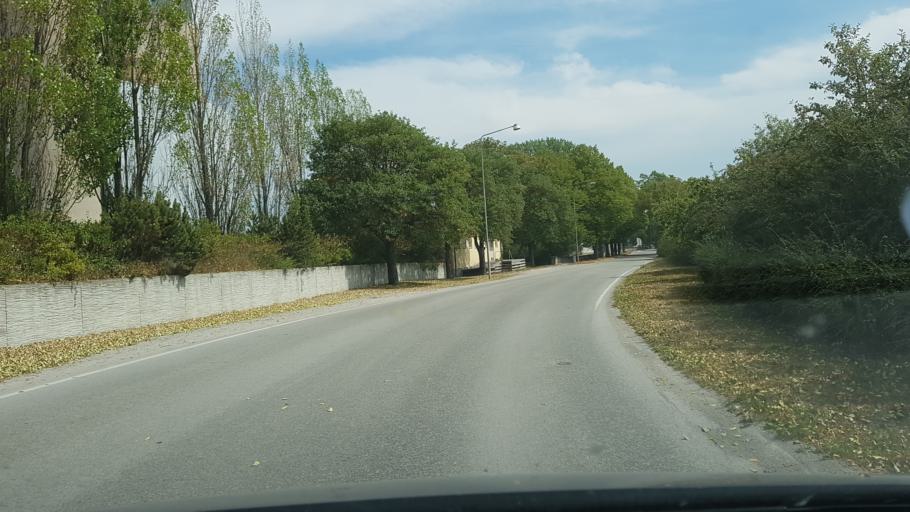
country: SE
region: Gotland
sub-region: Gotland
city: Slite
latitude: 57.7089
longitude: 18.7998
